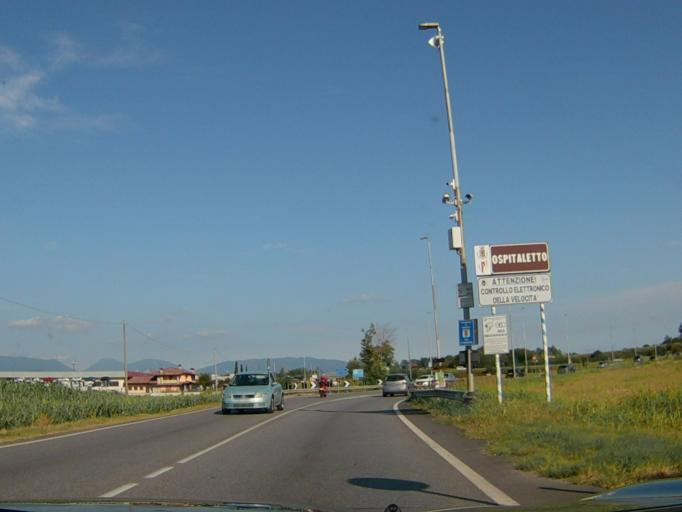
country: IT
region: Lombardy
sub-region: Provincia di Brescia
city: Lodetto
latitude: 45.5572
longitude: 10.0531
